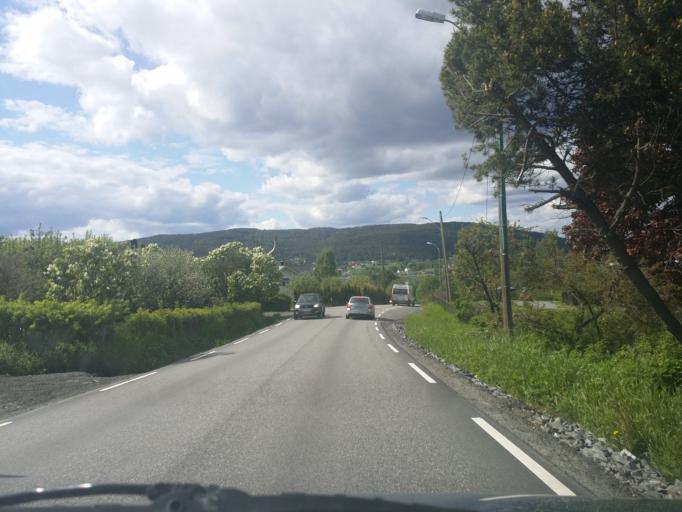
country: NO
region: Oppland
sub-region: Jevnaker
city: Jevnaker
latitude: 60.2372
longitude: 10.4044
